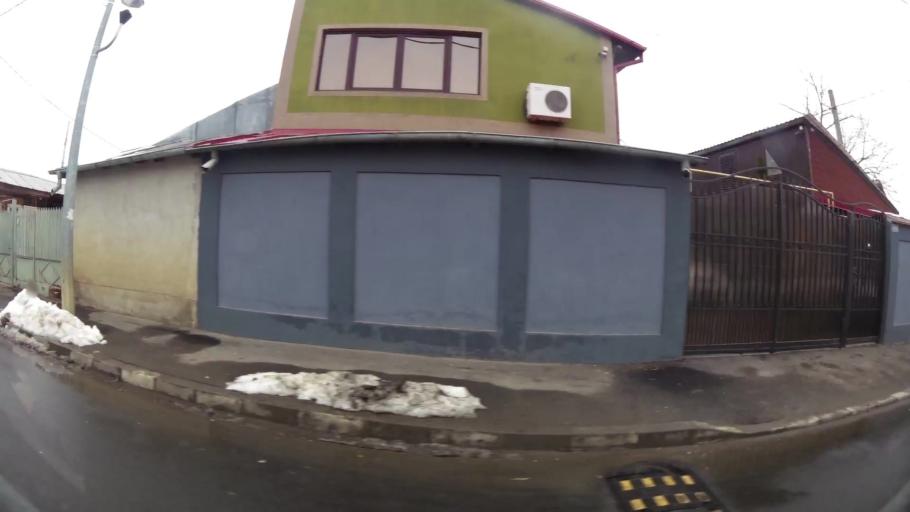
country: RO
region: Ilfov
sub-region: Comuna Pantelimon
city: Pantelimon
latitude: 44.4521
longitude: 26.1976
